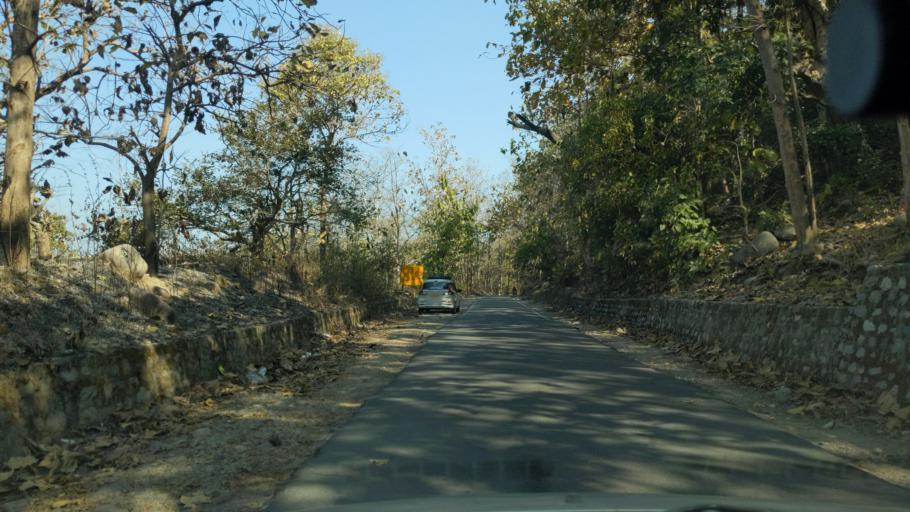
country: IN
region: Uttarakhand
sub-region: Naini Tal
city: Ramnagar
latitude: 29.4000
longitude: 79.1353
